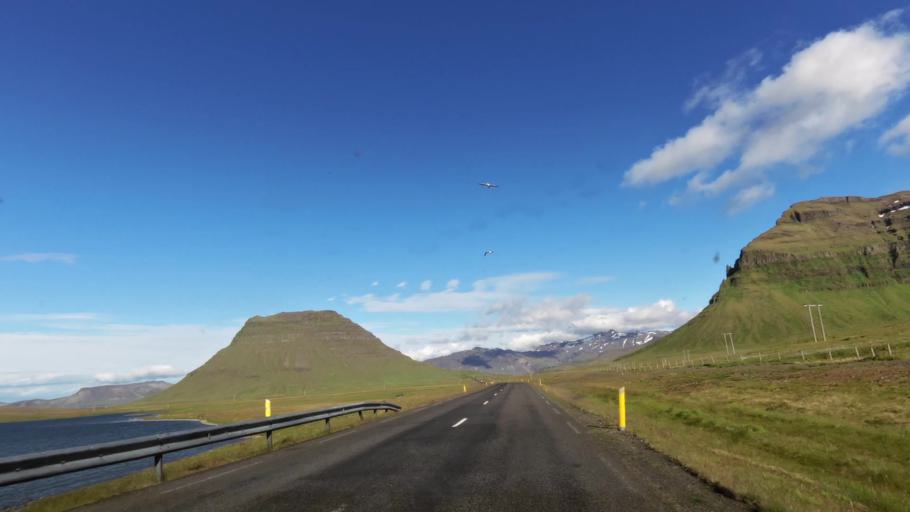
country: IS
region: West
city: Olafsvik
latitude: 64.9425
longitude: -23.3801
